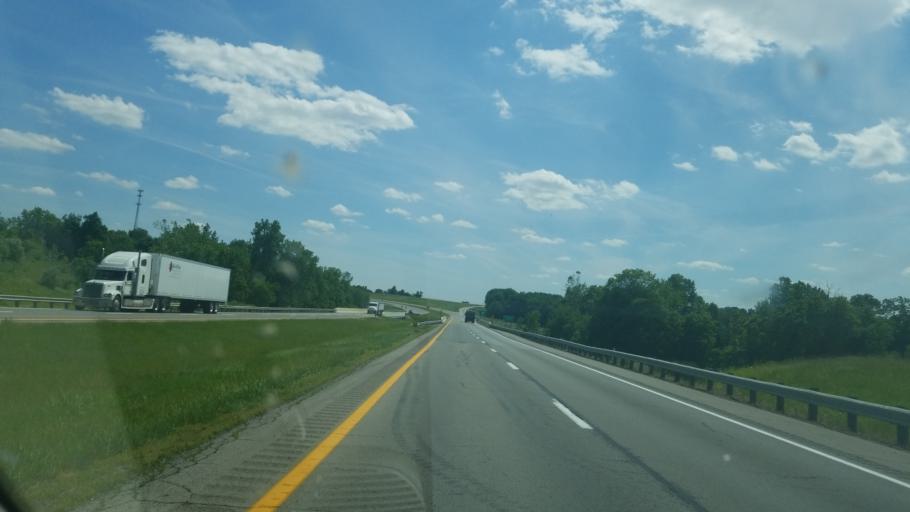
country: US
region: Ohio
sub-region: Wyandot County
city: Upper Sandusky
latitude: 40.7898
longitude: -83.2413
